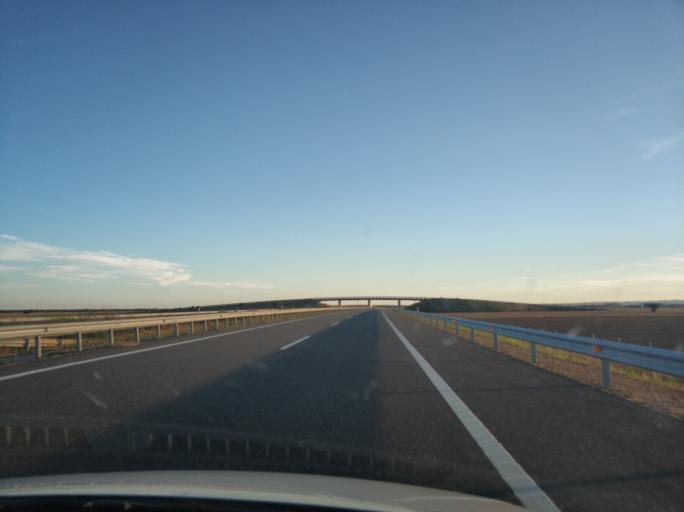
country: ES
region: Castille and Leon
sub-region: Provincia de Zamora
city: Barcial del Barco
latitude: 41.9362
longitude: -5.6444
